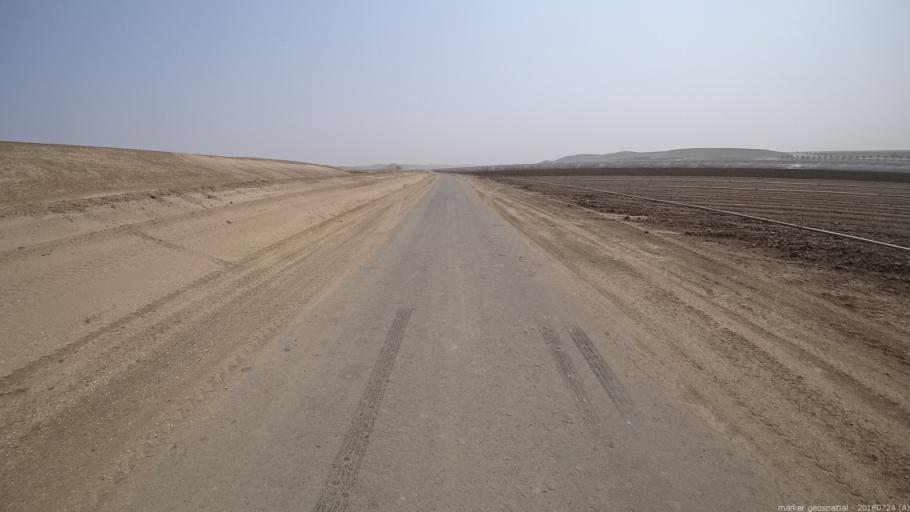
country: US
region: California
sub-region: Monterey County
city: King City
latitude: 36.1640
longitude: -121.0279
